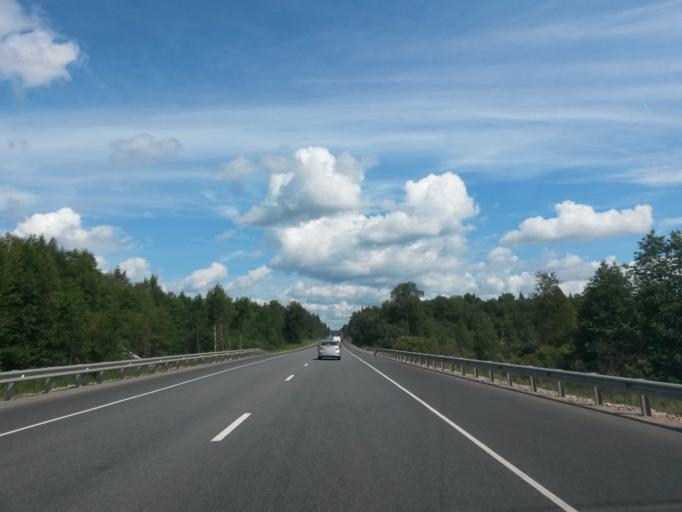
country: RU
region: Jaroslavl
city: Pereslavl'-Zalesskiy
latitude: 56.8322
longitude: 38.9163
